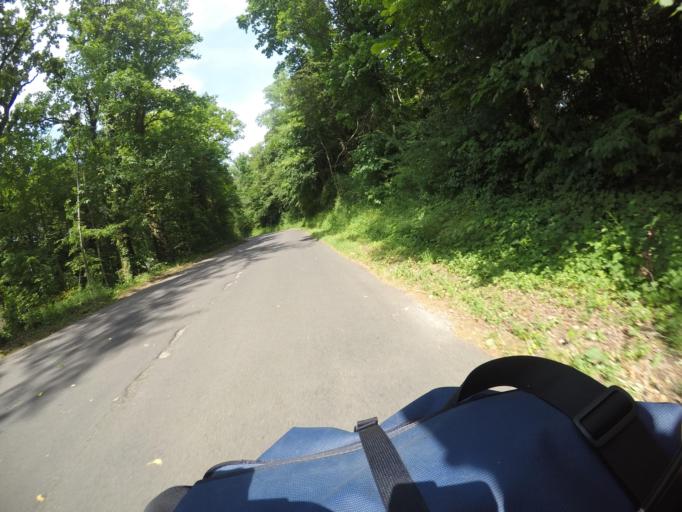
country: DE
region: Baden-Wuerttemberg
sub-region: Karlsruhe Region
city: Weingarten
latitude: 48.9934
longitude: 8.4942
